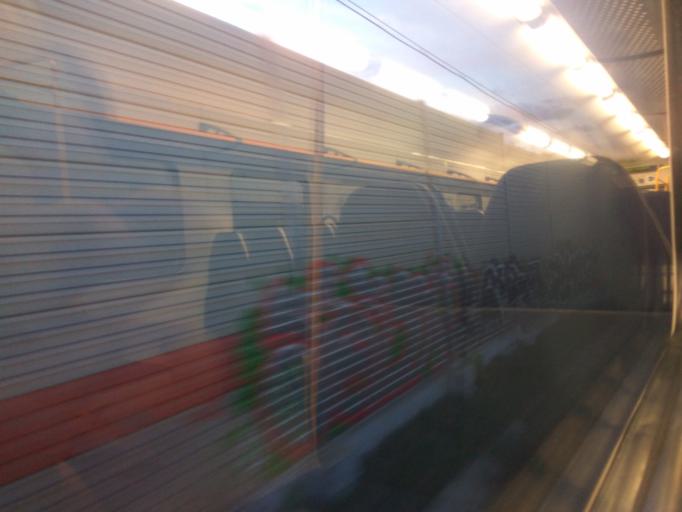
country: RU
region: Moscow
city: Solntsevo
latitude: 55.6533
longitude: 37.3809
